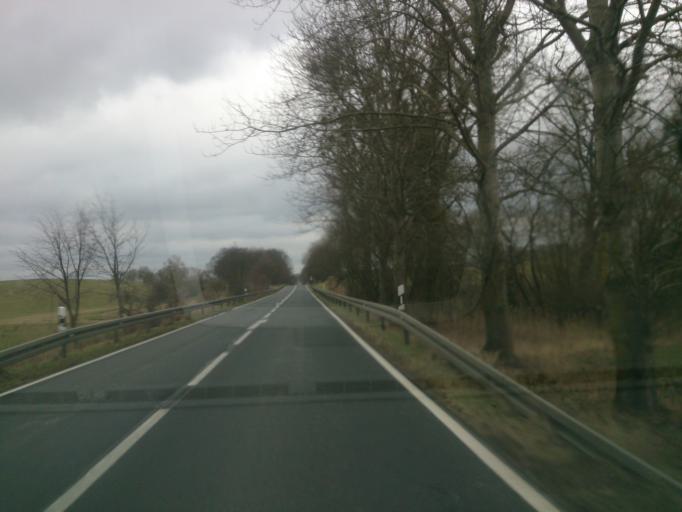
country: DE
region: Mecklenburg-Vorpommern
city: Mollenhagen
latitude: 53.5605
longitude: 12.8600
